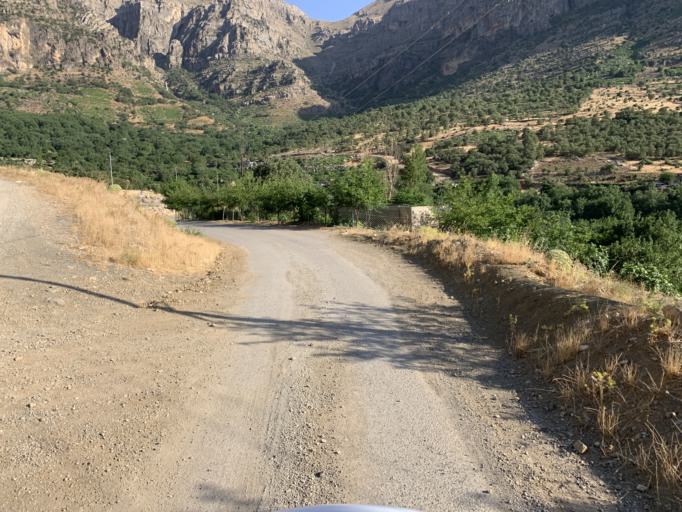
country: IQ
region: As Sulaymaniyah
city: Qeladize
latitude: 35.9911
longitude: 45.1996
